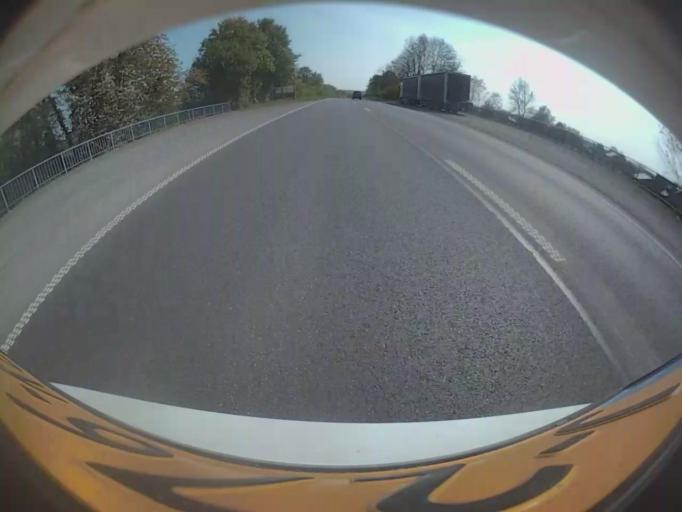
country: BE
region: Wallonia
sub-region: Province de Namur
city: Ciney
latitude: 50.3038
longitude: 5.1215
